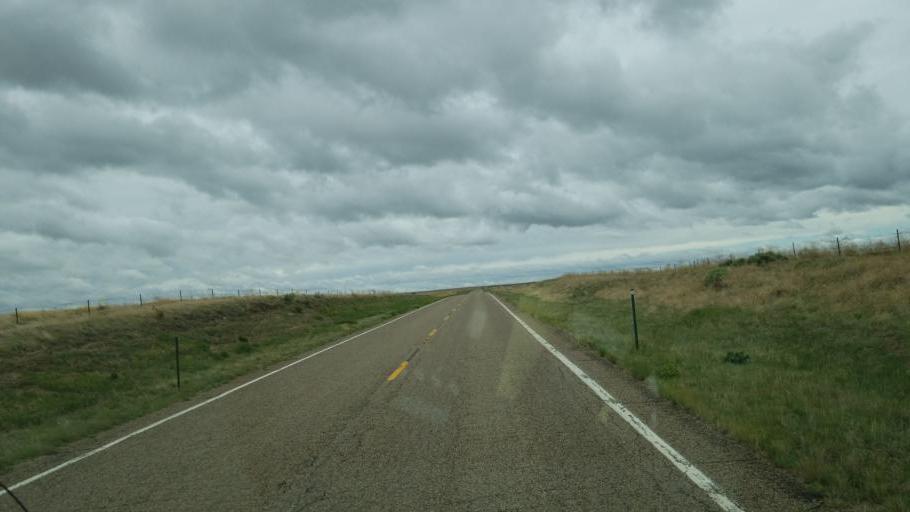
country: US
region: Colorado
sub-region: Lincoln County
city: Hugo
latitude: 38.8509
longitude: -103.6006
